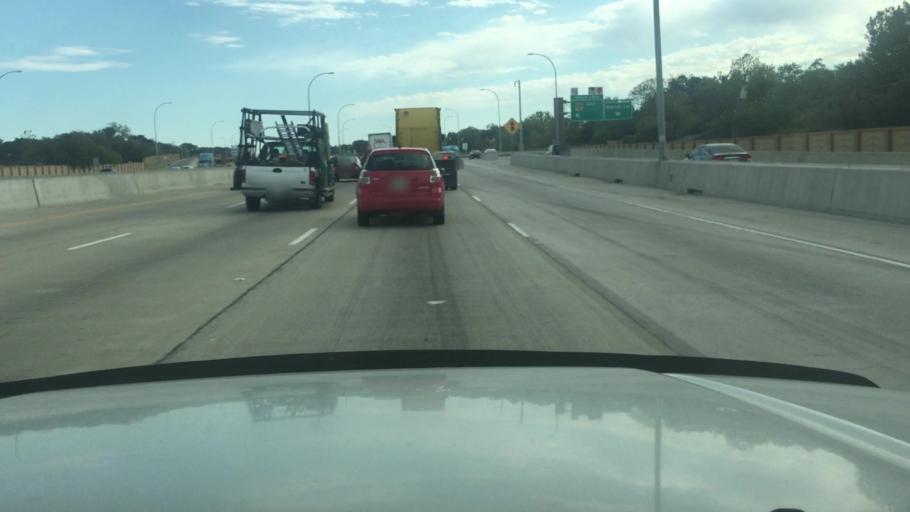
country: US
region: Texas
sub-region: Dallas County
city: Farmers Branch
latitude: 32.9160
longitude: -96.8611
